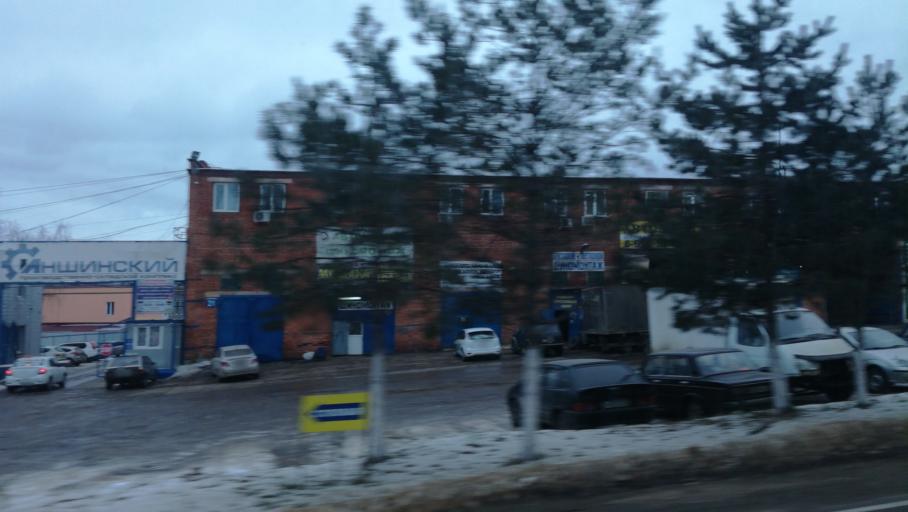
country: RU
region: Tula
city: Kosaya Gora
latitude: 54.1666
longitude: 37.4685
